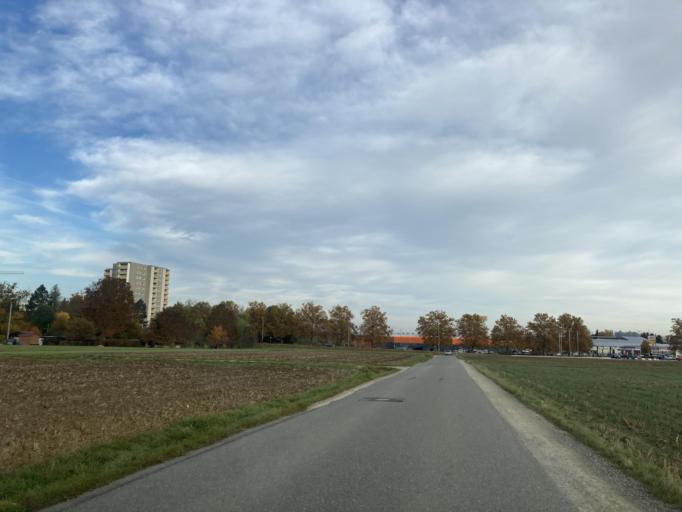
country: DE
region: Baden-Wuerttemberg
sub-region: Tuebingen Region
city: Ofterdingen
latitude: 48.4021
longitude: 9.0388
